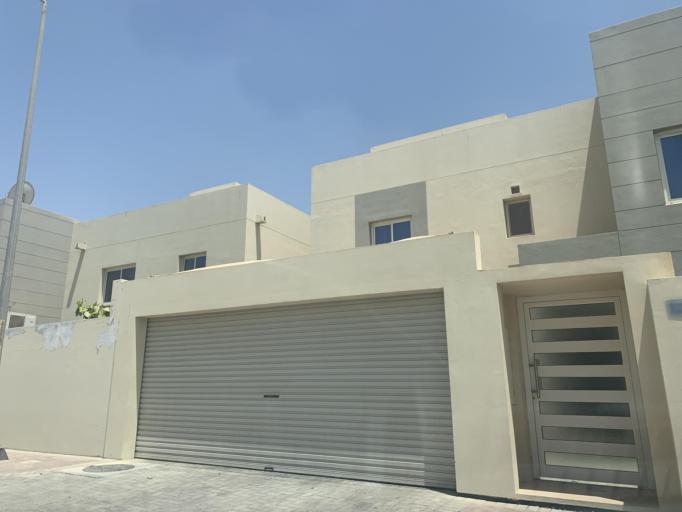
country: BH
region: Manama
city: Jidd Hafs
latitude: 26.2369
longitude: 50.4716
